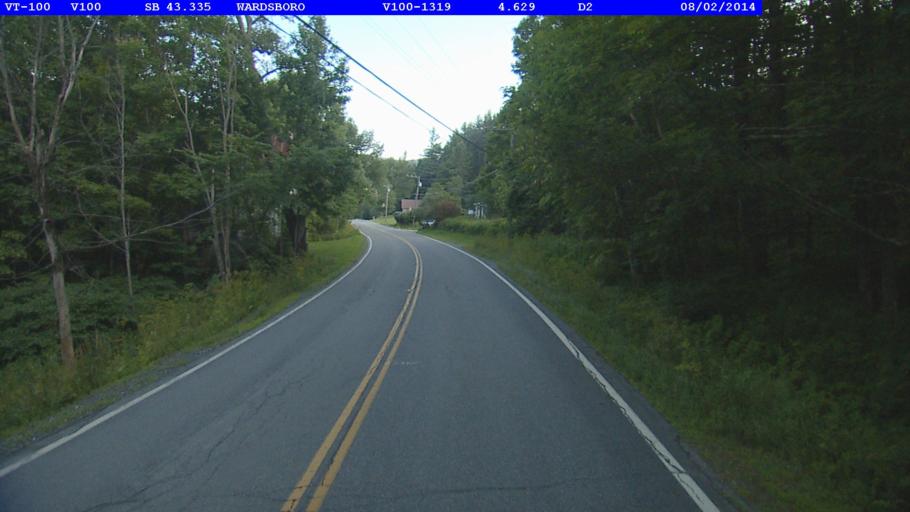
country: US
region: Vermont
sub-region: Windham County
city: Dover
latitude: 43.0312
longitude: -72.8189
